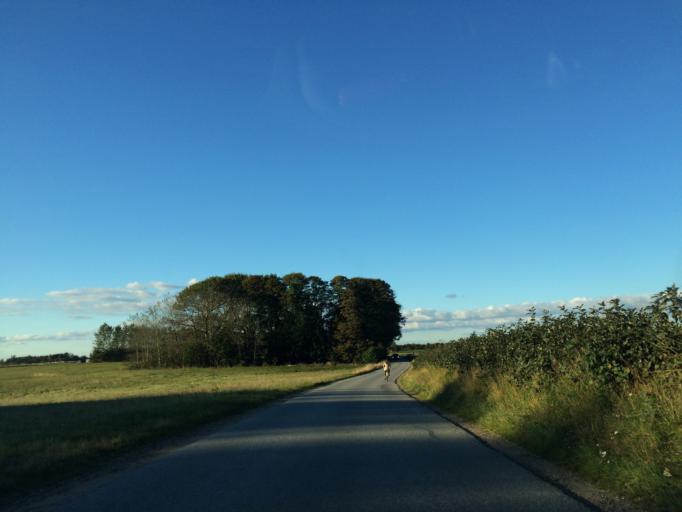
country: DK
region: Central Jutland
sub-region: Silkeborg Kommune
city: Svejbaek
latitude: 56.1777
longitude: 9.6931
